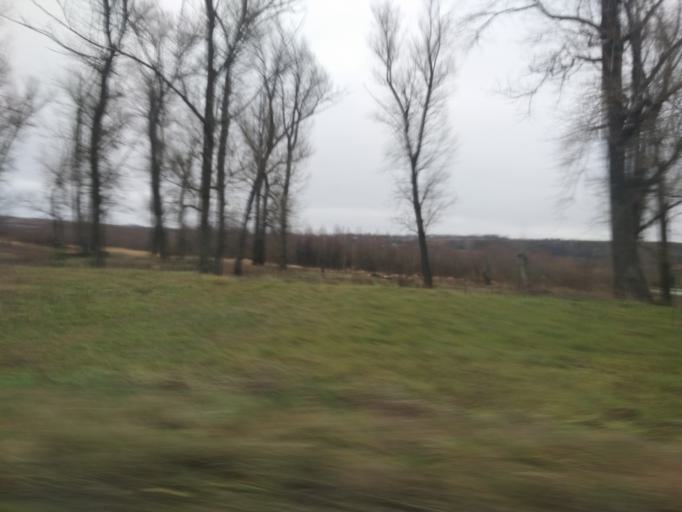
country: RU
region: Kirov
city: Krasnaya Polyana
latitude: 56.2465
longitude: 51.2009
